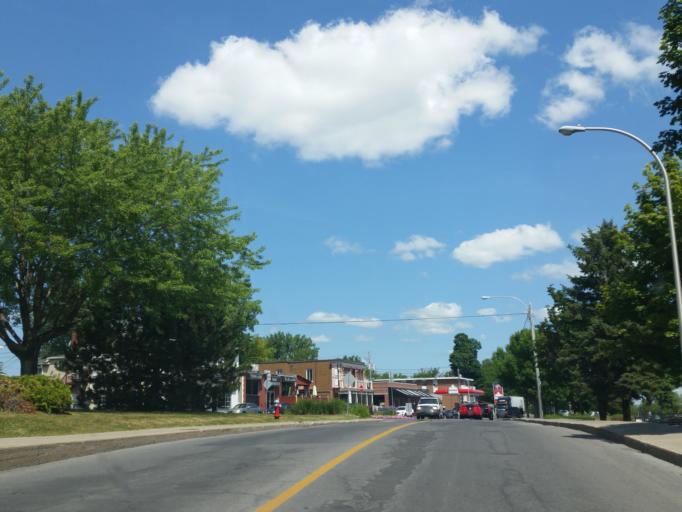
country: CA
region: Quebec
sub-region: Monteregie
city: Saint-Jean-sur-Richelieu
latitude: 45.3101
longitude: -73.2518
